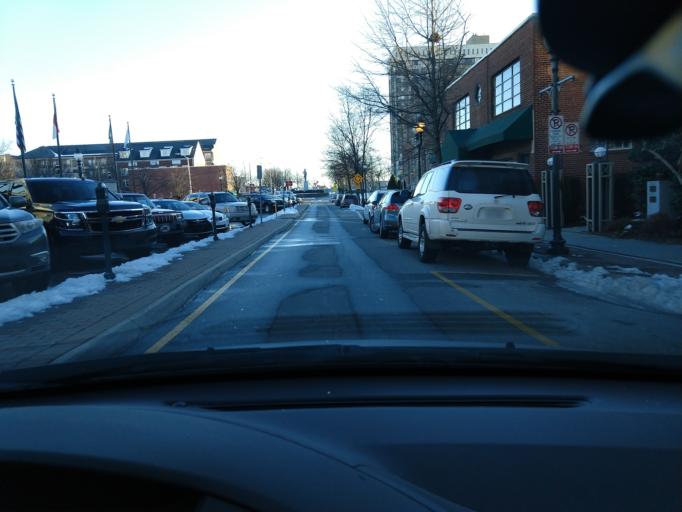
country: US
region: North Carolina
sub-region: Guilford County
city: Greensboro
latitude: 36.0698
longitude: -79.7918
